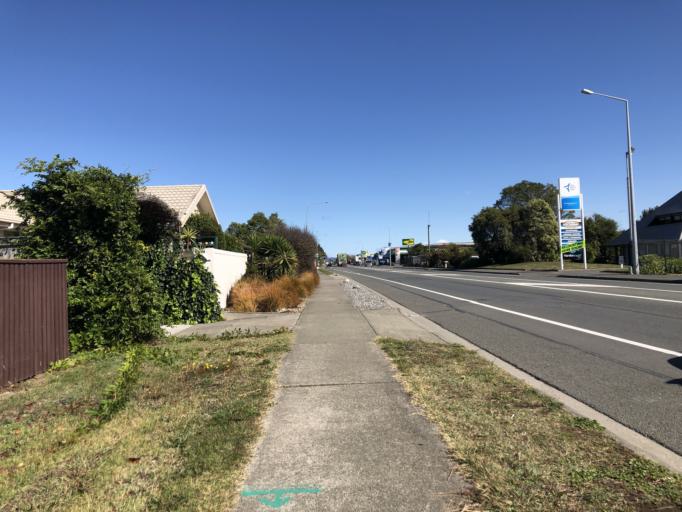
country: NZ
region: Tasman
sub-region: Tasman District
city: Richmond
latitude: -41.3431
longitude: 173.1715
